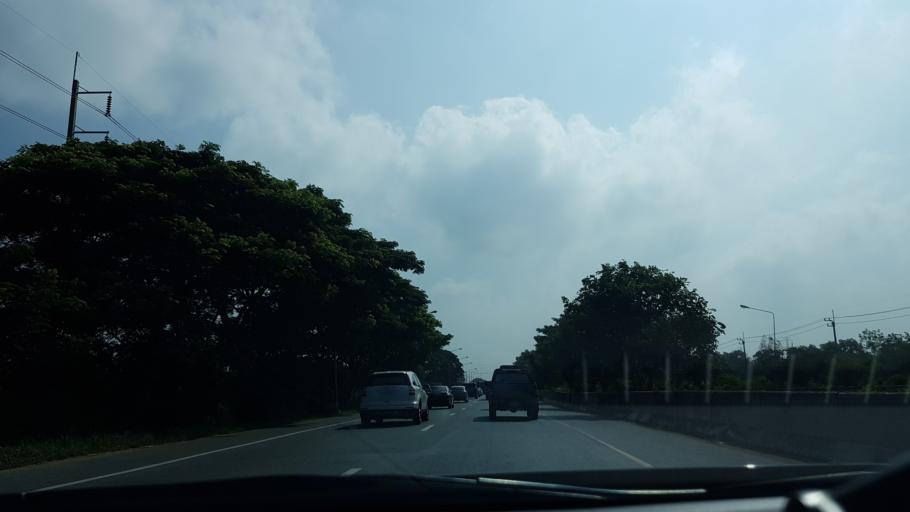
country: TH
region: Phra Nakhon Si Ayutthaya
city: Bang Pa-in
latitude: 14.1695
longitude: 100.6007
